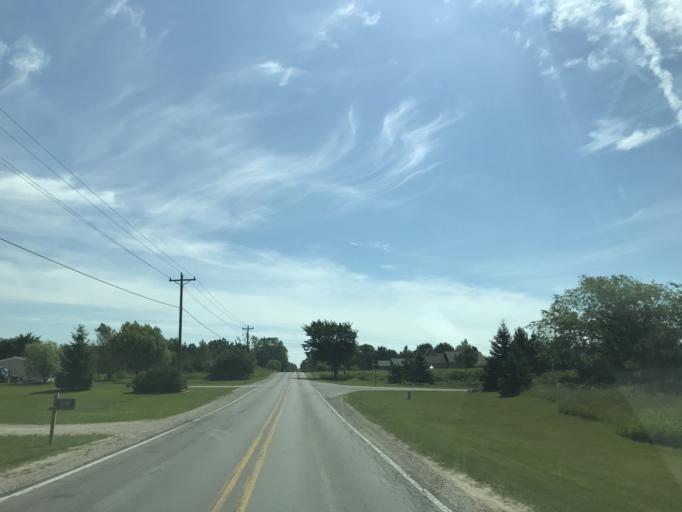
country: US
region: Michigan
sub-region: Grand Traverse County
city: Traverse City
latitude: 44.6576
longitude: -85.6731
